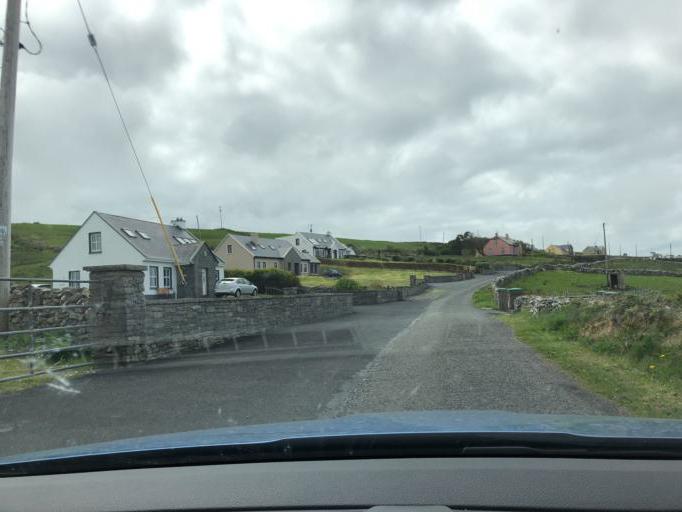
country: IE
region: Connaught
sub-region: County Galway
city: Bearna
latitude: 52.9974
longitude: -9.3997
